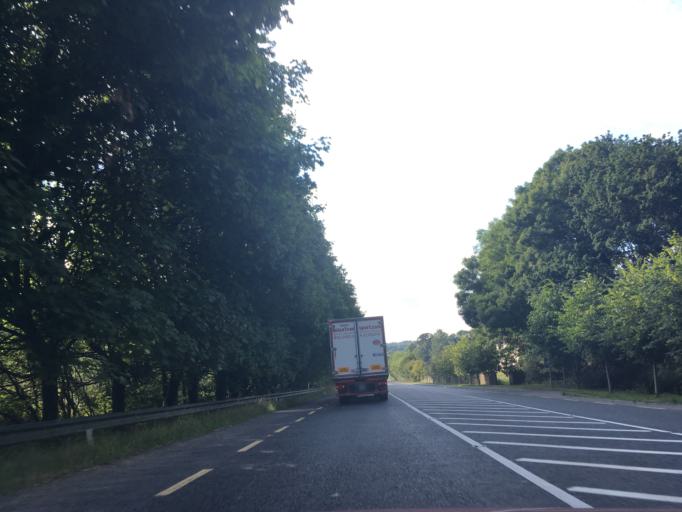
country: IE
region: Leinster
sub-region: Loch Garman
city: New Ross
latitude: 52.3830
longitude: -6.9451
